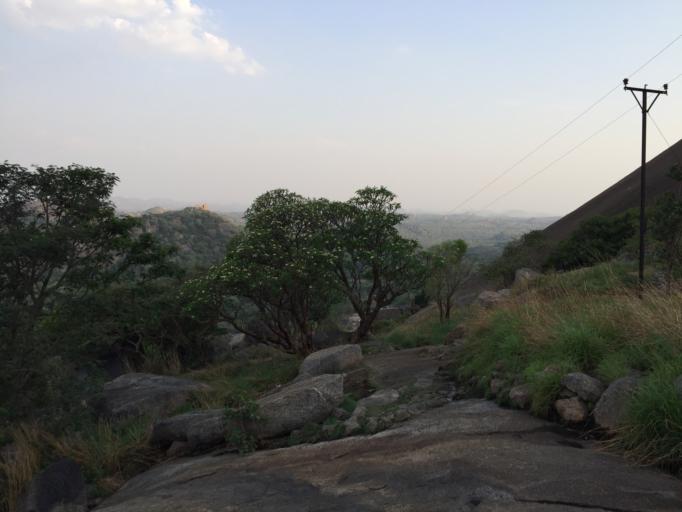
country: IN
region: Karnataka
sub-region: Ramanagara
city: Magadi
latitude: 12.9218
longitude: 77.2981
